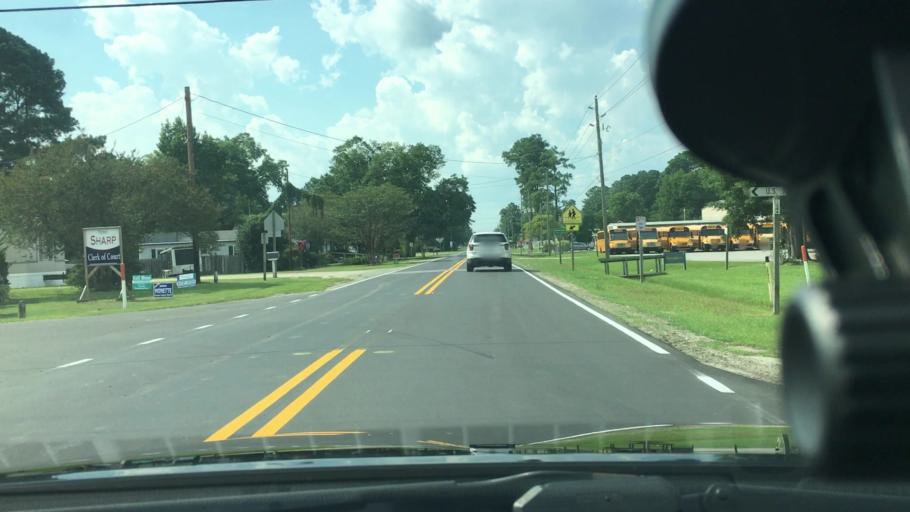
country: US
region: North Carolina
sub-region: Craven County
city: James City
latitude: 35.0677
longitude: -77.0184
